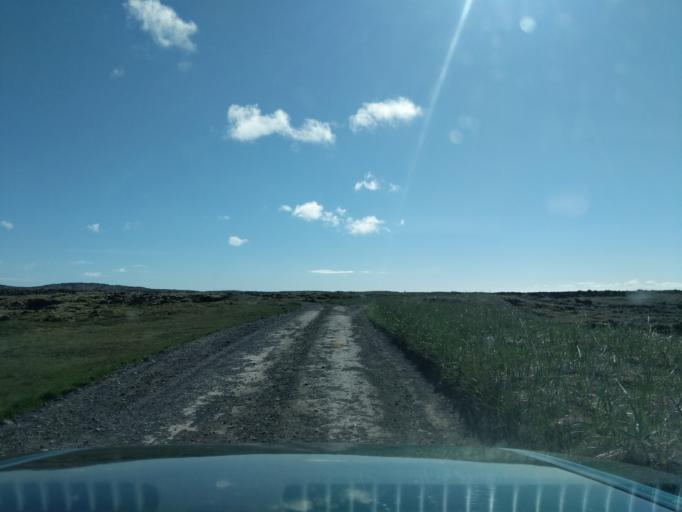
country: IS
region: West
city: Olafsvik
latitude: 64.8772
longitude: -23.9946
